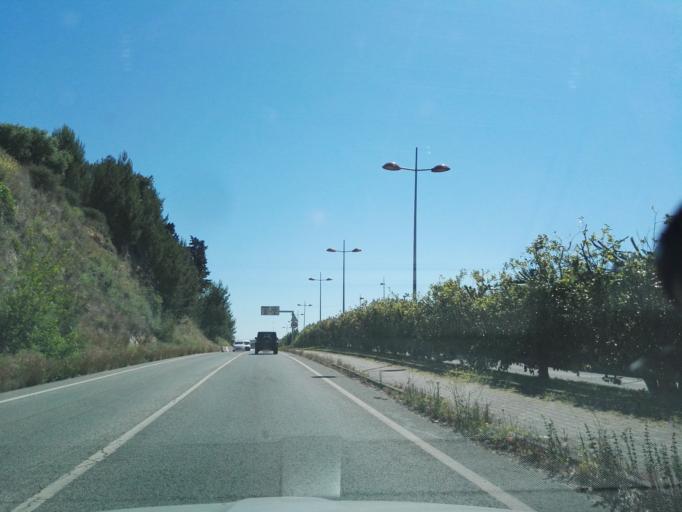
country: PT
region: Lisbon
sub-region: Loures
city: Bobadela
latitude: 38.7993
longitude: -9.1020
